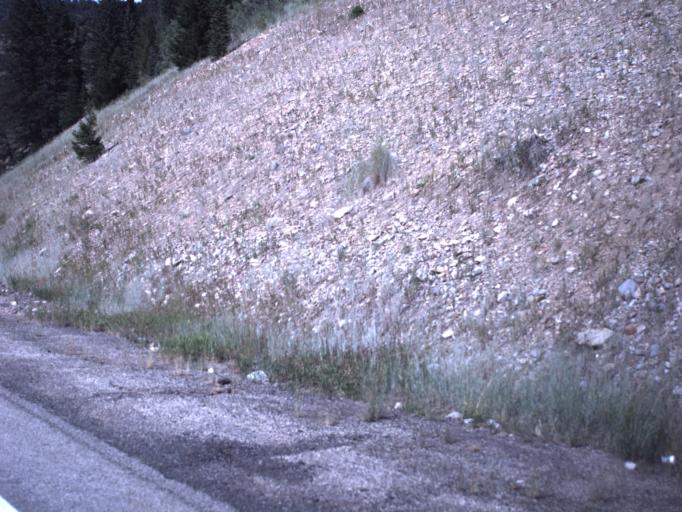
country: US
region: Utah
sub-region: Wasatch County
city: Heber
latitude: 40.3340
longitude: -111.2613
